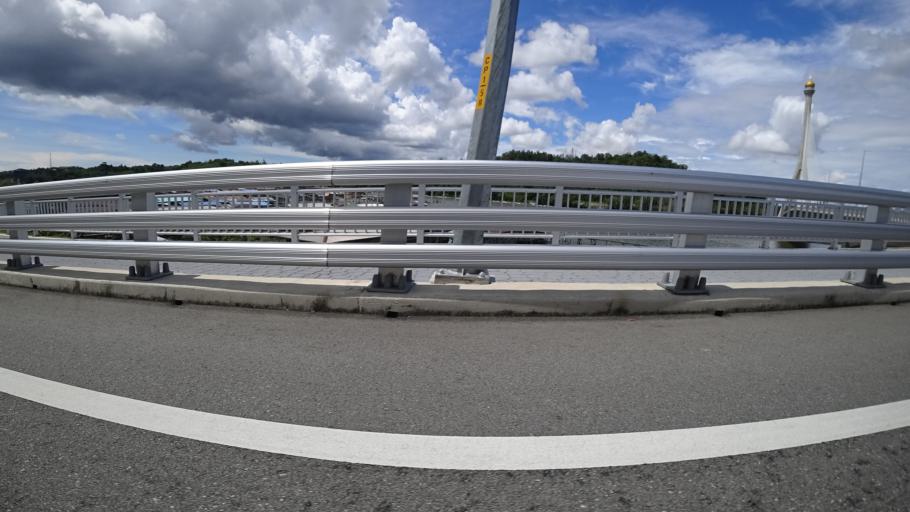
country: BN
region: Brunei and Muara
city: Bandar Seri Begawan
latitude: 4.8775
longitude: 114.9460
